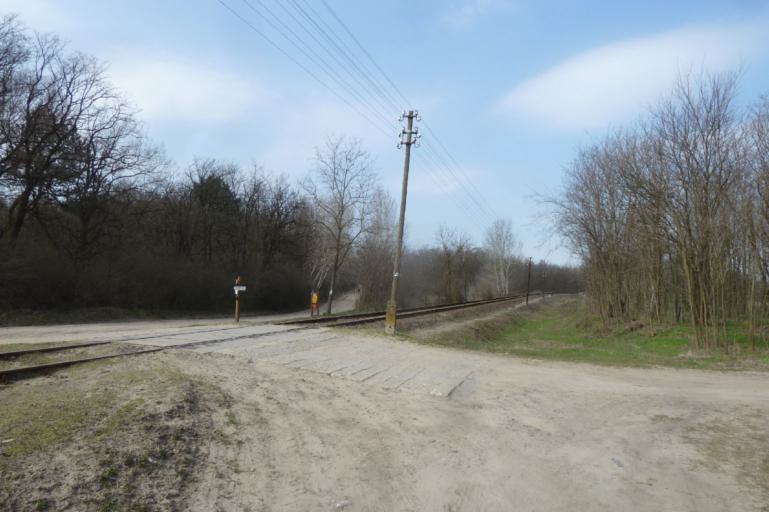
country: HU
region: Bacs-Kiskun
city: Lajosmizse
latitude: 46.9436
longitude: 19.5854
